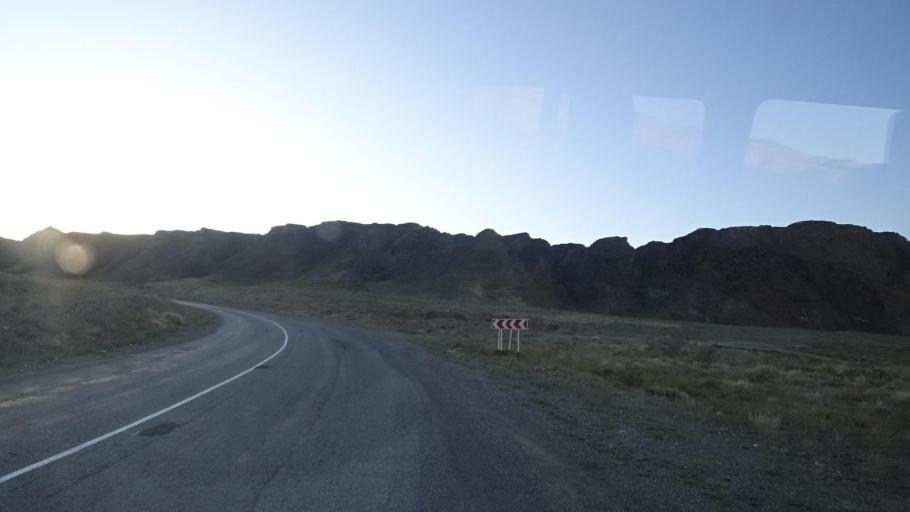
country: KZ
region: Almaty Oblysy
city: Kegen
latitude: 43.2718
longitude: 78.9711
